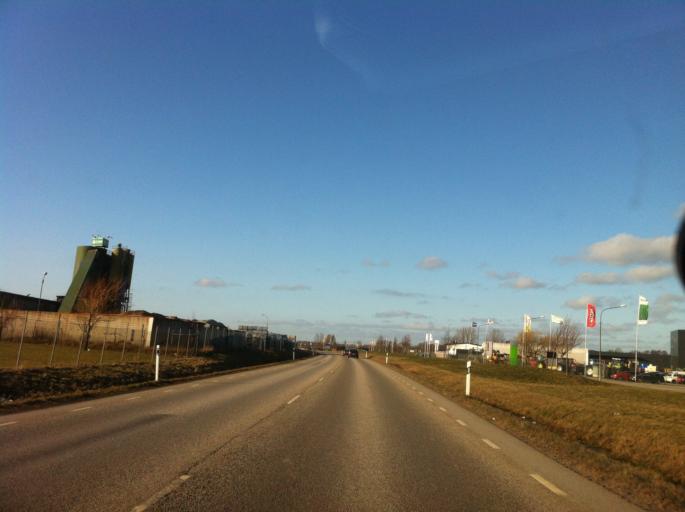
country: SE
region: Skane
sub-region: Svedala Kommun
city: Klagerup
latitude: 55.5607
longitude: 13.2559
